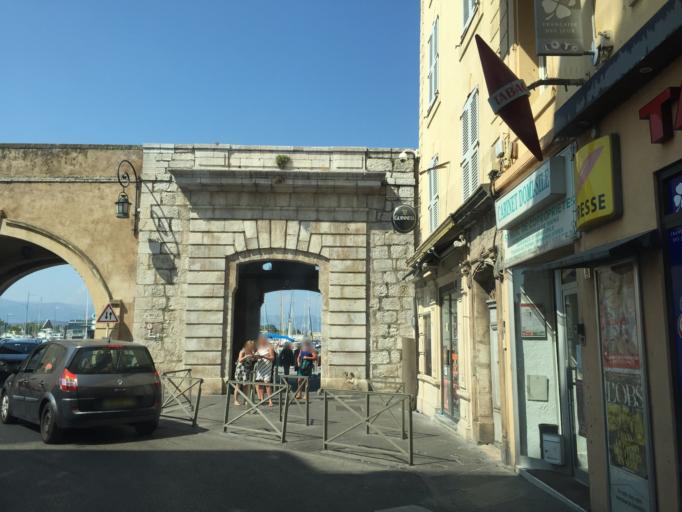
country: FR
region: Provence-Alpes-Cote d'Azur
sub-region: Departement des Alpes-Maritimes
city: Antibes
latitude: 43.5828
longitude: 7.1280
